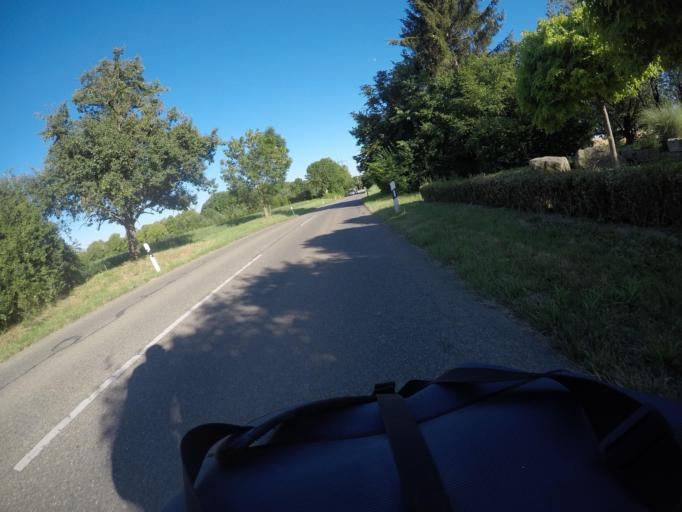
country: DE
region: Baden-Wuerttemberg
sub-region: Regierungsbezirk Stuttgart
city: Stuttgart Muehlhausen
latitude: 48.8890
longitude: 9.2383
